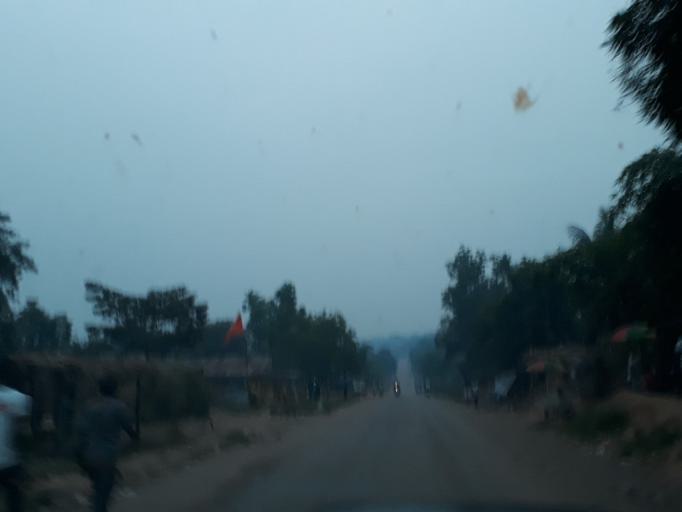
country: CD
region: Bandundu
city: Kikwit
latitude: -5.0560
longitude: 18.8537
